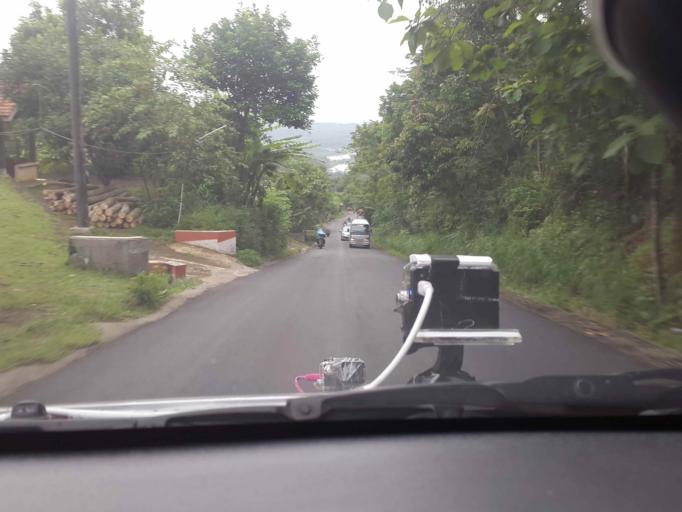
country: ID
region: Central Java
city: Banyumas
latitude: -7.5408
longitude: 109.3134
